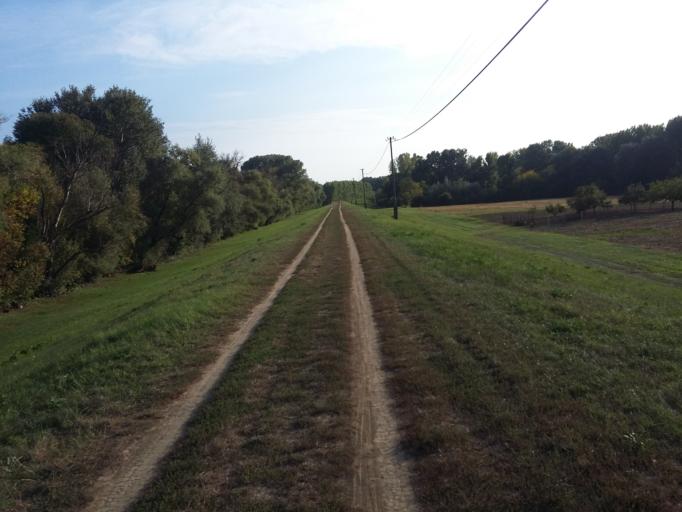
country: HU
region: Csongrad
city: Szeged
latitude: 46.2096
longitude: 20.1184
